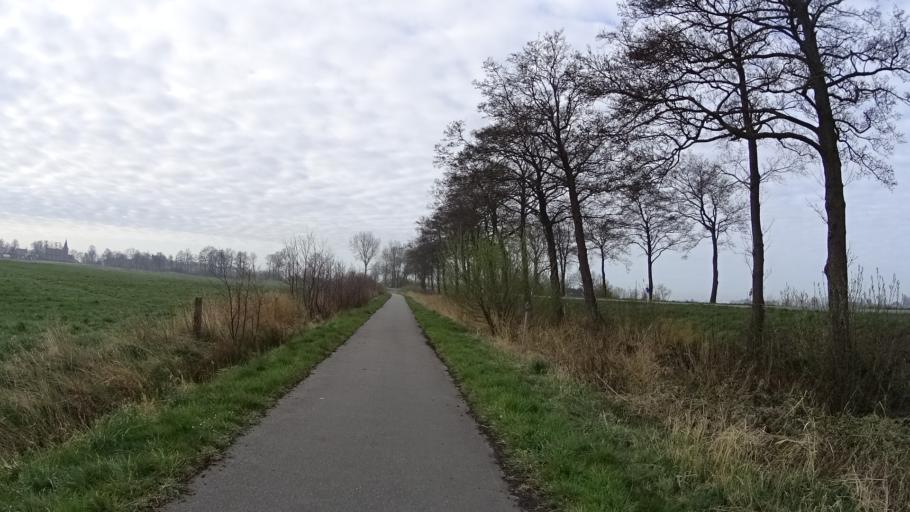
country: DE
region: Lower Saxony
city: Upgant-Schott
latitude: 53.4292
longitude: 7.3193
